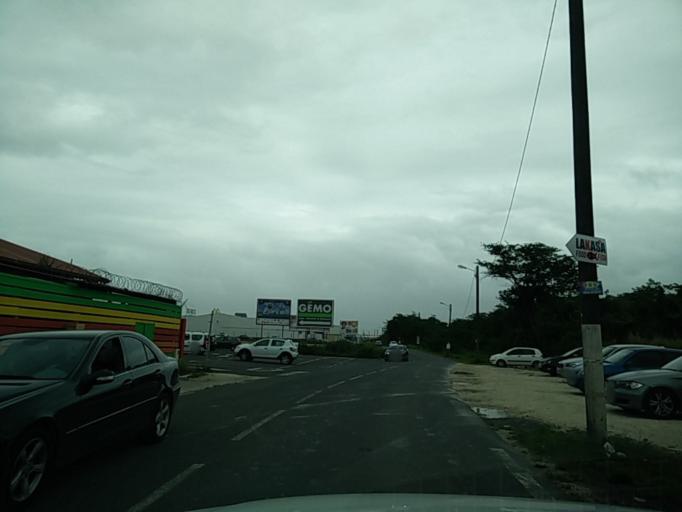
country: GP
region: Guadeloupe
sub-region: Guadeloupe
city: Baie-Mahault
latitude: 16.2533
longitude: -61.5672
